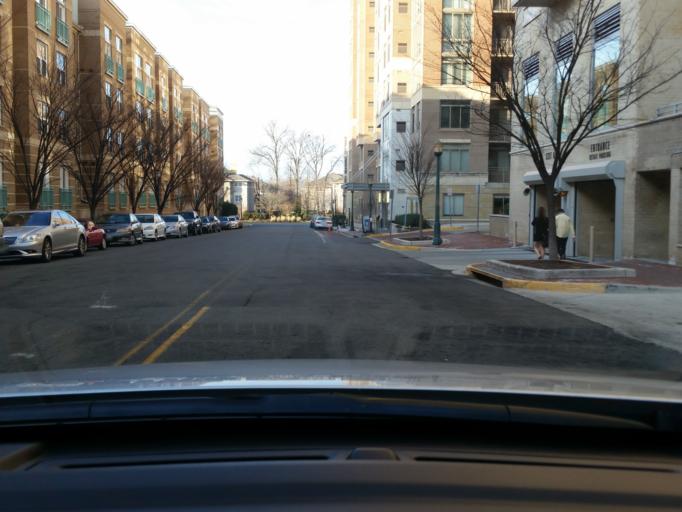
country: US
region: Virginia
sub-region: Fairfax County
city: Reston
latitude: 38.9590
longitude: -77.3617
